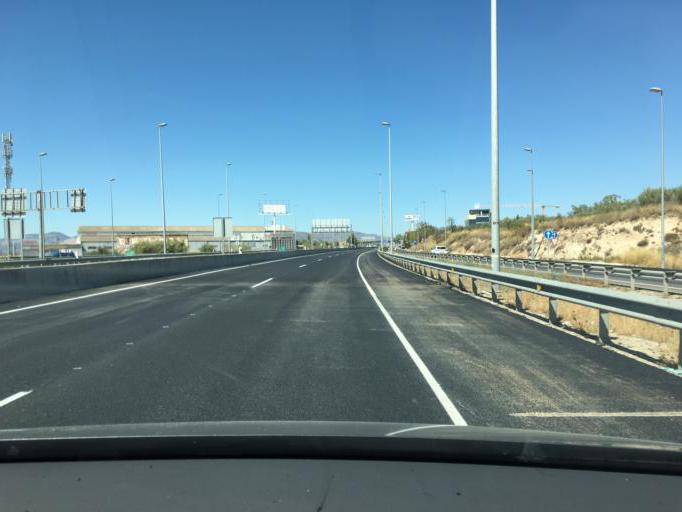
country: ES
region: Andalusia
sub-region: Provincia de Granada
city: Albolote
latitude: 37.2422
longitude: -3.6524
